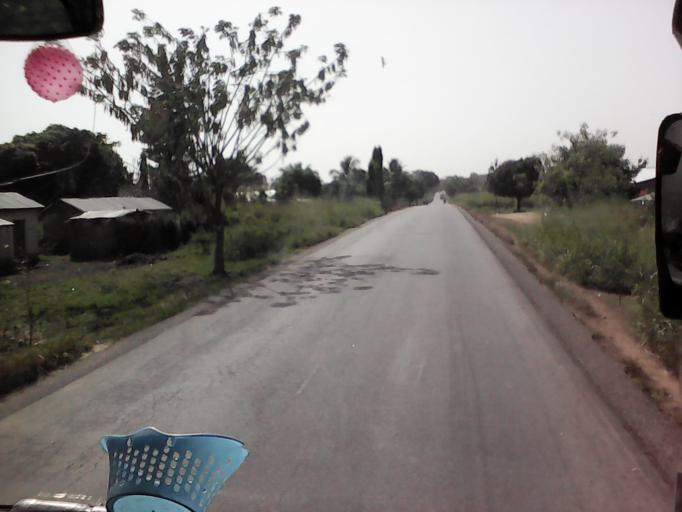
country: TG
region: Centrale
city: Sokode
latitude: 8.8389
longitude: 1.0746
